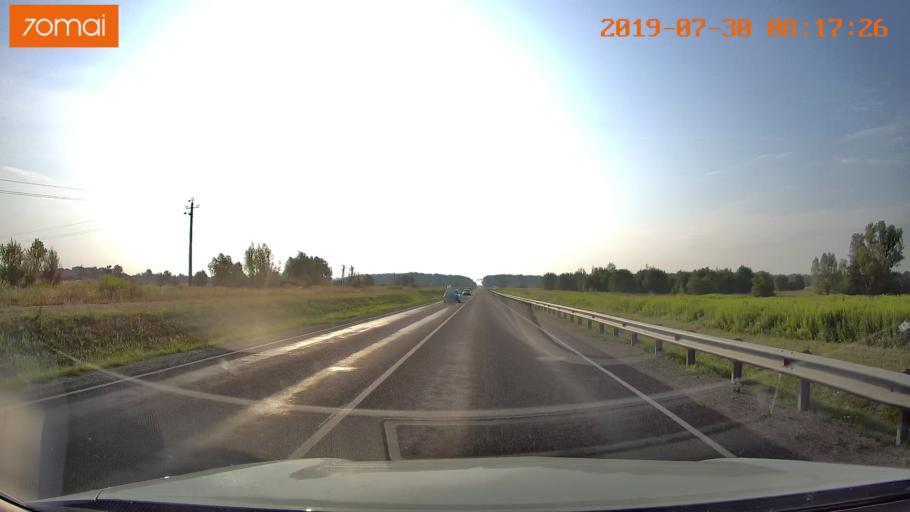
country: RU
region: Kaliningrad
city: Zheleznodorozhnyy
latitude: 54.6364
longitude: 21.4375
